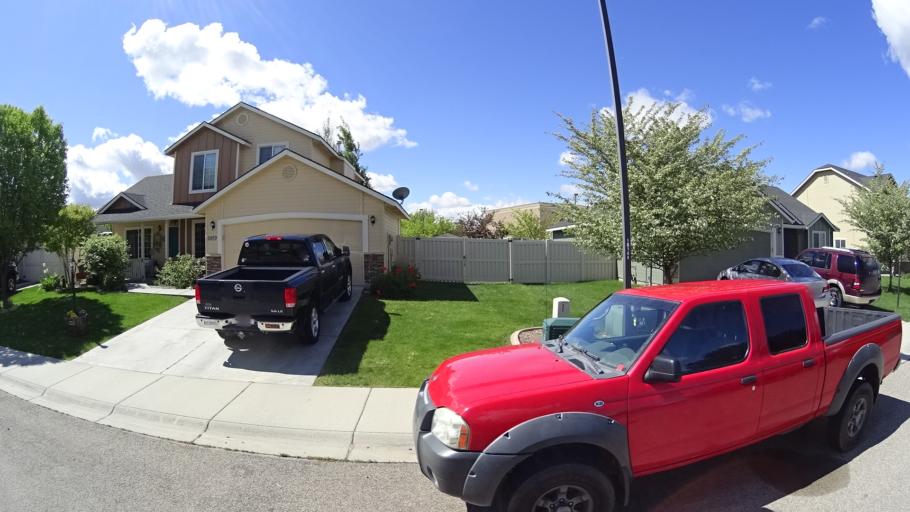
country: US
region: Idaho
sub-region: Ada County
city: Kuna
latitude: 43.5083
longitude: -116.4443
